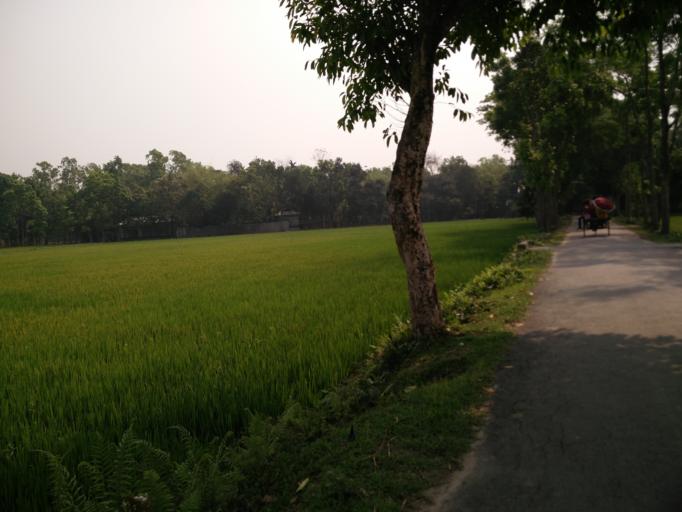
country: BD
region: Dhaka
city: Muktagacha
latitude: 24.9151
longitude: 90.2225
